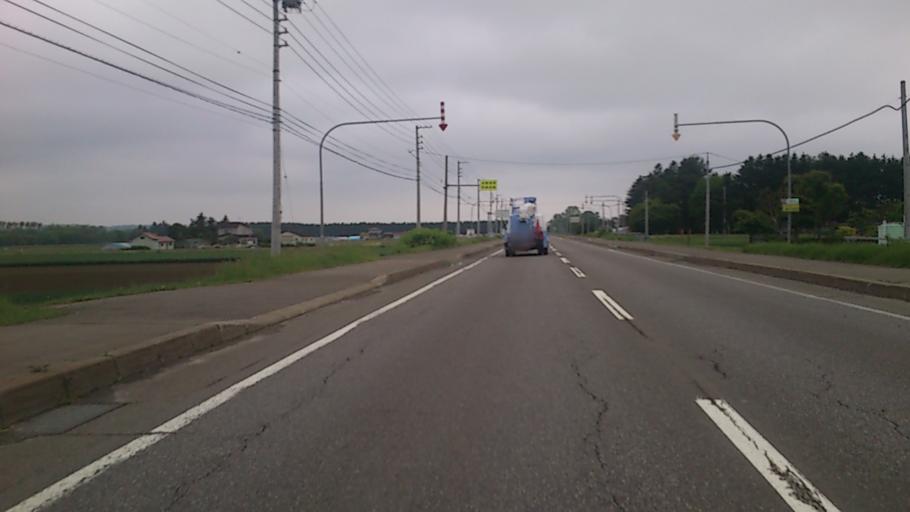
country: JP
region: Hokkaido
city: Obihiro
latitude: 42.9210
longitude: 143.3308
